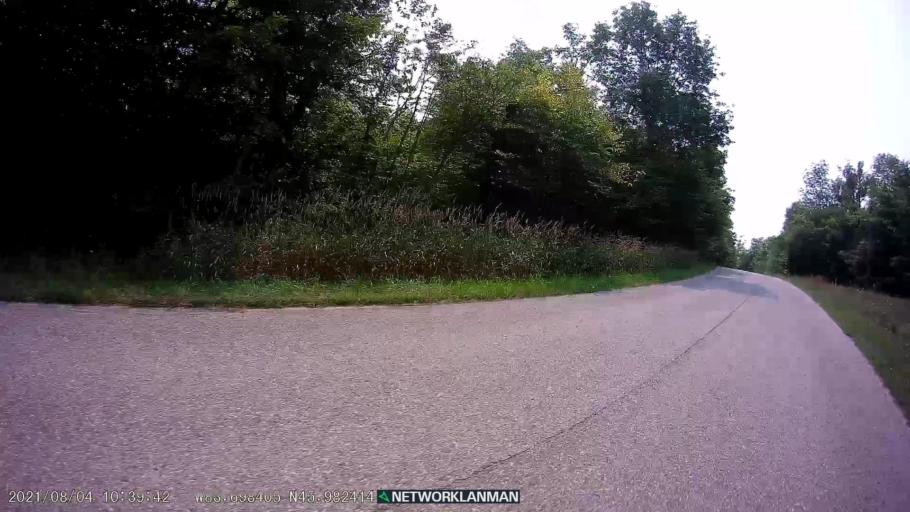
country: CA
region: Ontario
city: Thessalon
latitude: 45.9820
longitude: -83.6988
